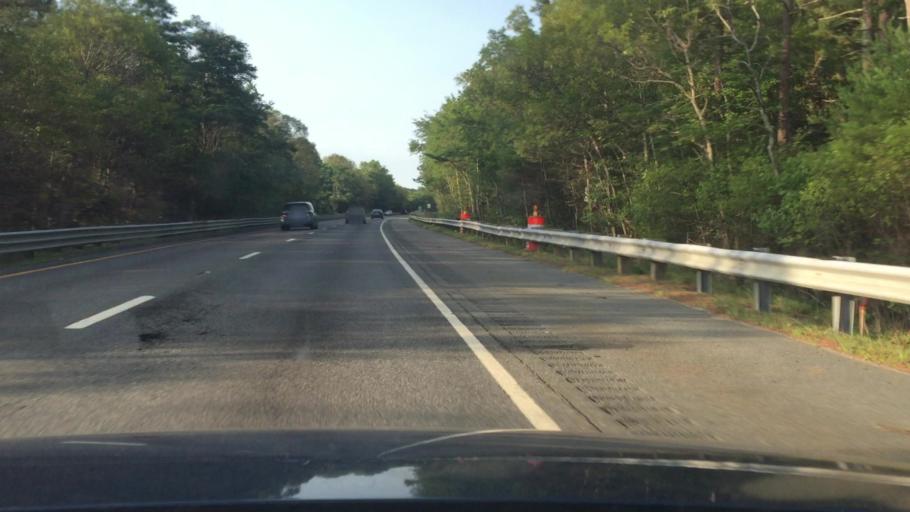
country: US
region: Massachusetts
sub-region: Plymouth County
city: South Duxbury
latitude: 42.0468
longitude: -70.7234
